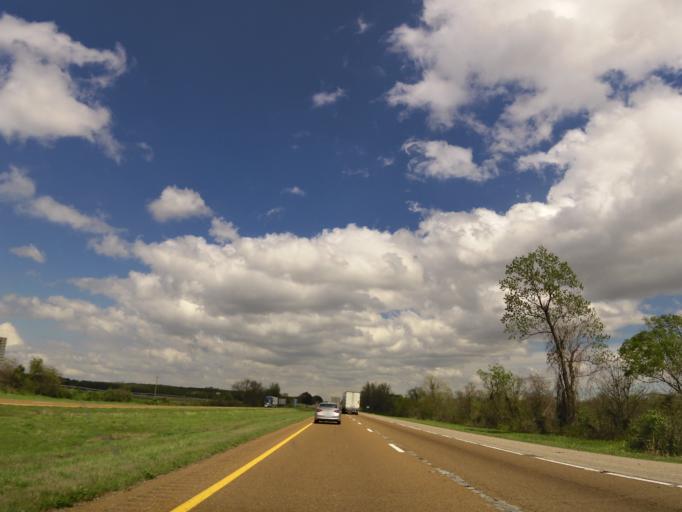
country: US
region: Tennessee
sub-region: Tipton County
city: Mason
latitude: 35.3563
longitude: -89.5020
